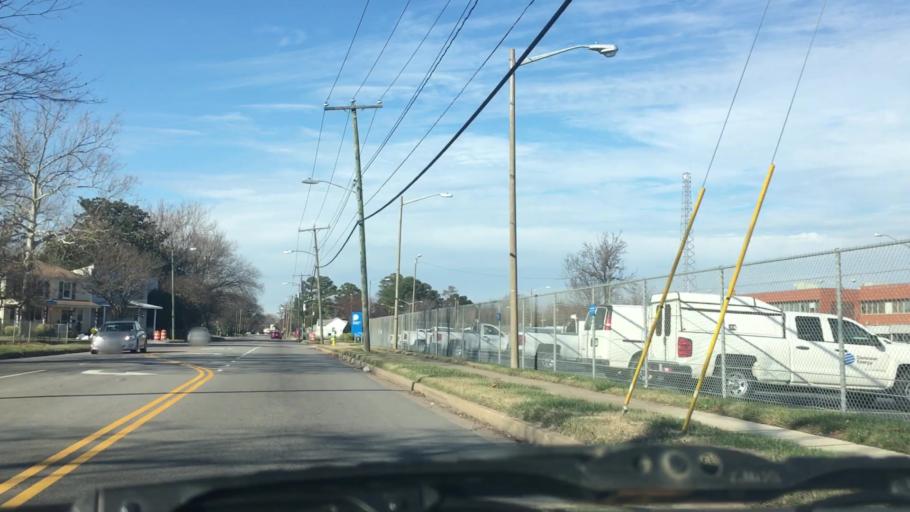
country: US
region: Virginia
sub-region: City of Norfolk
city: Norfolk
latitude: 36.8793
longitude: -76.2537
